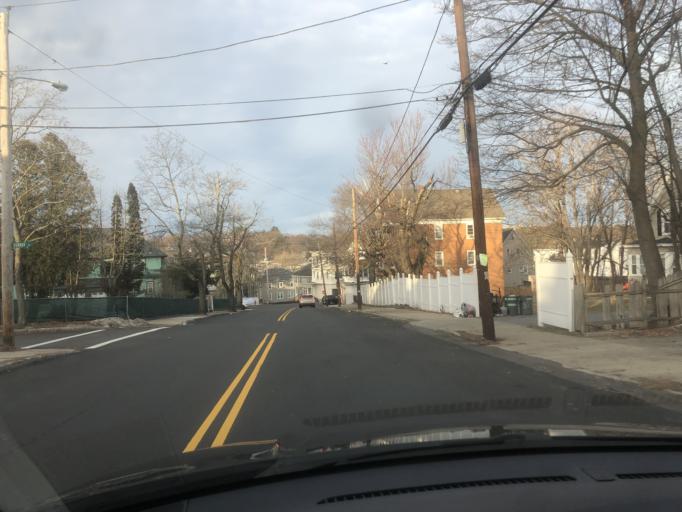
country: US
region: Massachusetts
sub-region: Essex County
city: Lawrence
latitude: 42.7216
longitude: -71.1548
